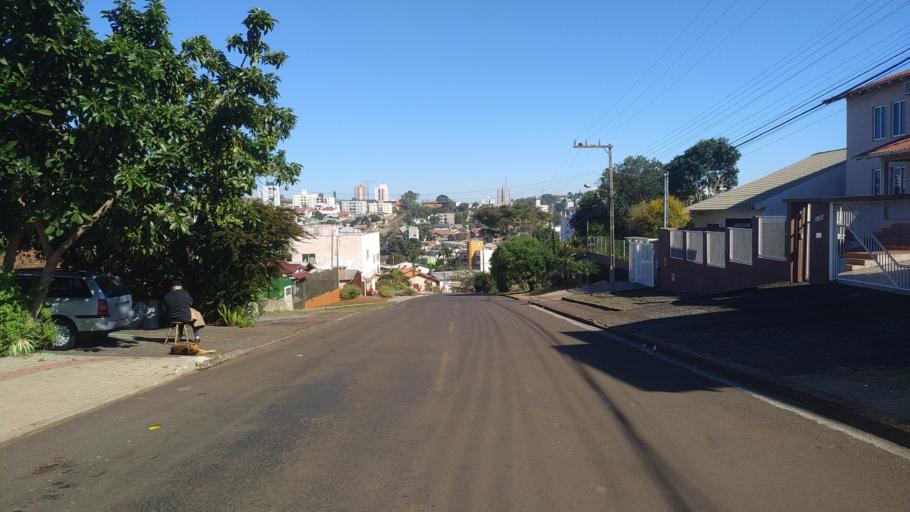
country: BR
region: Santa Catarina
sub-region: Chapeco
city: Chapeco
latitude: -27.1123
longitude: -52.5998
